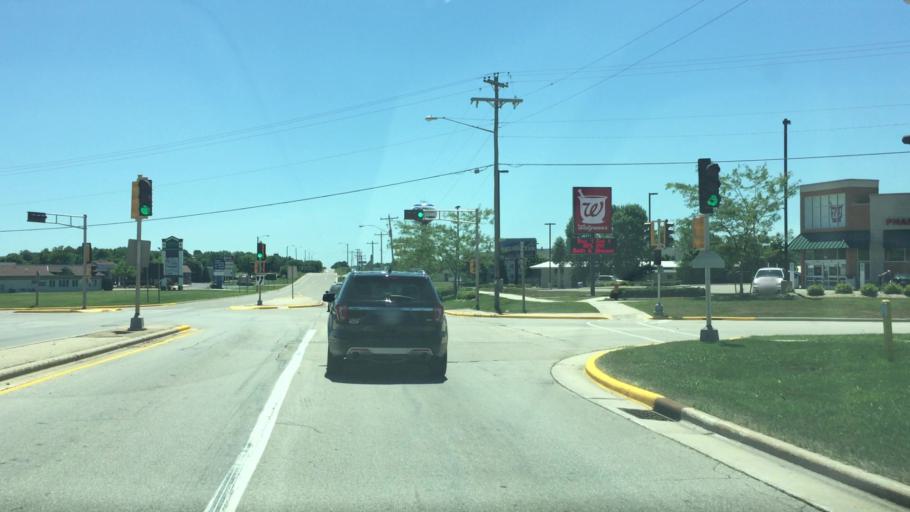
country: US
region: Wisconsin
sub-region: Calumet County
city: Chilton
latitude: 44.0228
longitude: -88.1555
